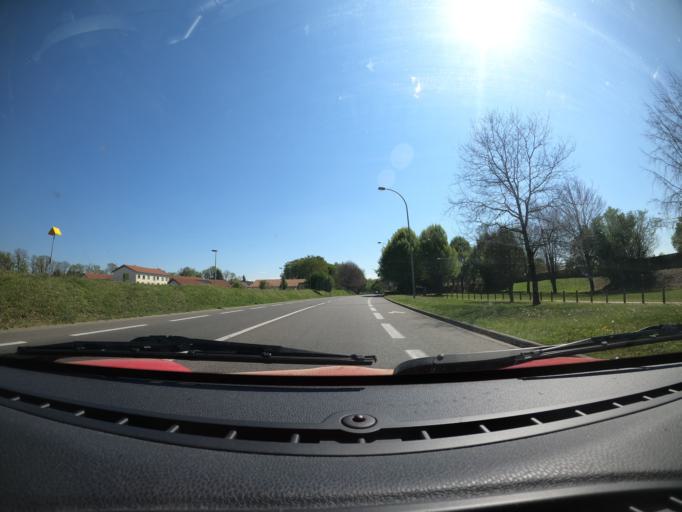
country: FR
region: Aquitaine
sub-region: Departement des Pyrenees-Atlantiques
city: Lons
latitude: 43.3386
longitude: -0.3853
